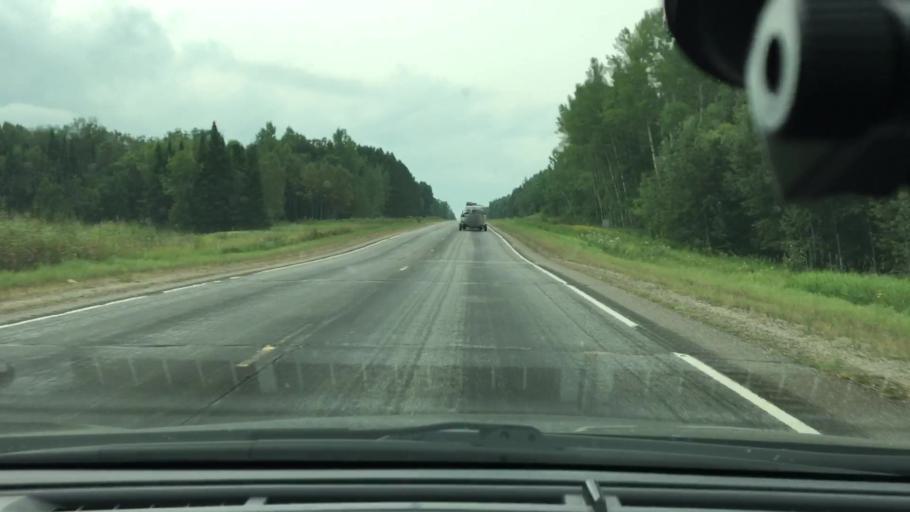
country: US
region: Minnesota
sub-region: Crow Wing County
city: Cross Lake
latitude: 46.6477
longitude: -93.9529
